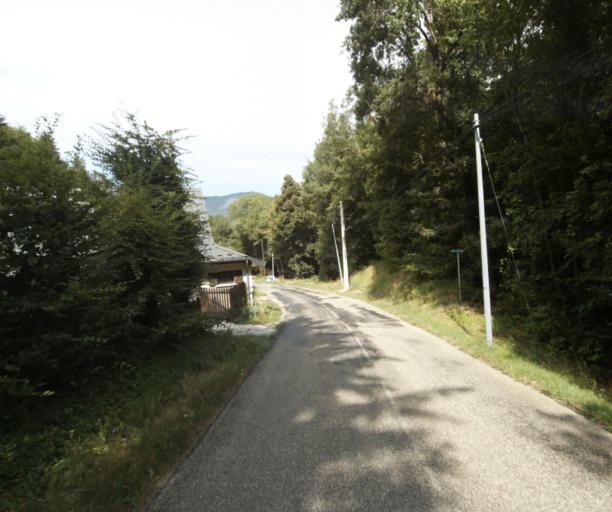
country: FR
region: Rhone-Alpes
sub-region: Departement de l'Isere
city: Le Sappey-en-Chartreuse
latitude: 45.2499
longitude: 5.7384
